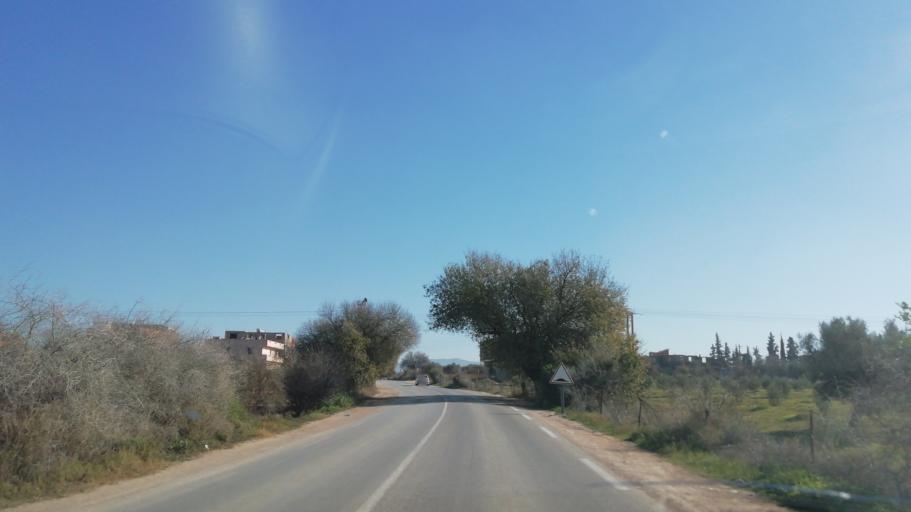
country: DZ
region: Tlemcen
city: Nedroma
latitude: 34.8316
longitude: -1.6945
